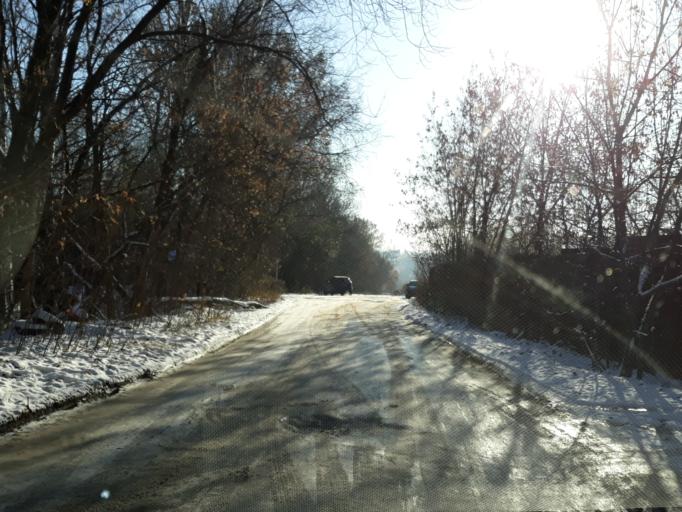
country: RU
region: Nizjnij Novgorod
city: Nizhniy Novgorod
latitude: 56.2560
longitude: 44.0040
